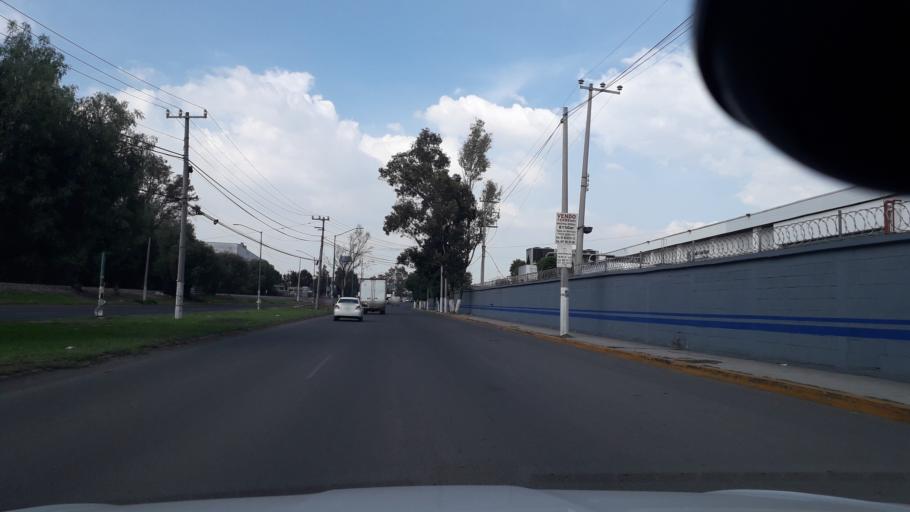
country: MX
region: Mexico
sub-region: Tultitlan
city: Buenavista
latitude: 19.6208
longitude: -99.1855
